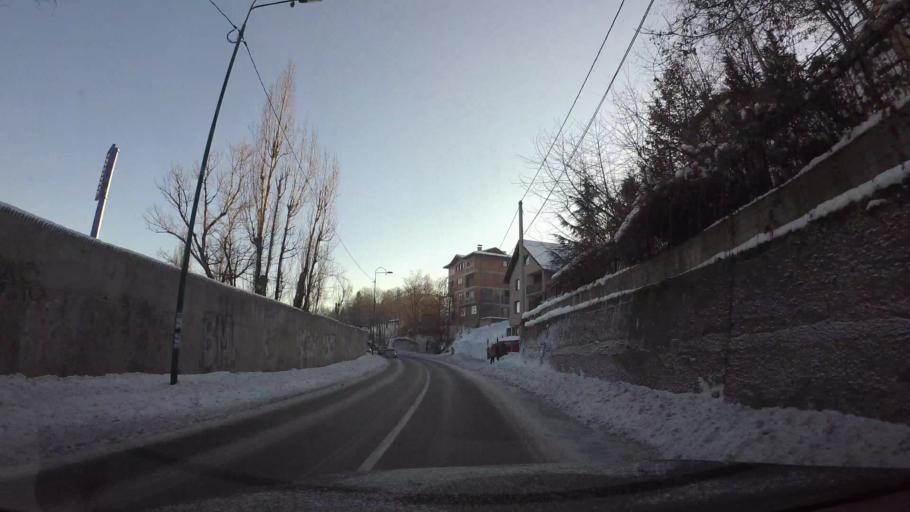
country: BA
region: Federation of Bosnia and Herzegovina
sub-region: Kanton Sarajevo
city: Sarajevo
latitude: 43.8456
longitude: 18.3875
